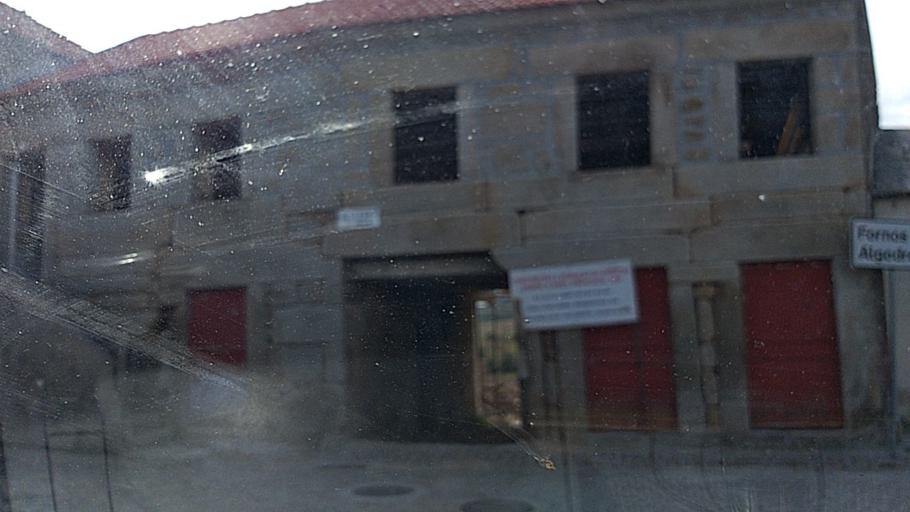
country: PT
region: Guarda
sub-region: Fornos de Algodres
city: Fornos de Algodres
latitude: 40.6819
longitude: -7.5299
